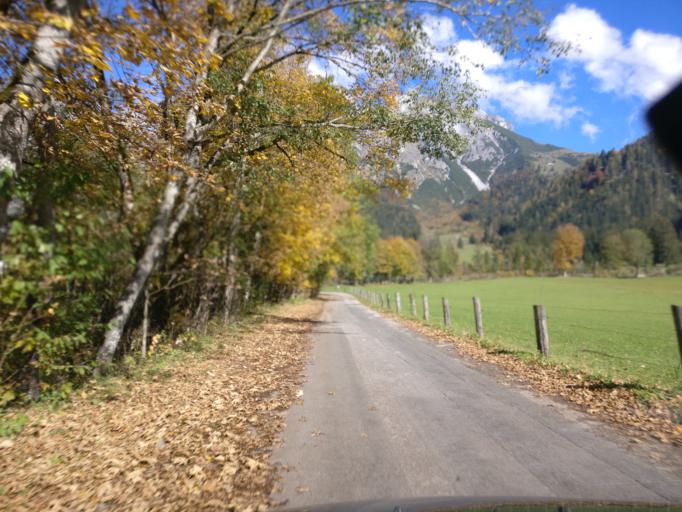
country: AT
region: Salzburg
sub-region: Politischer Bezirk Sankt Johann im Pongau
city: Werfenweng
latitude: 47.4732
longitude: 13.2678
